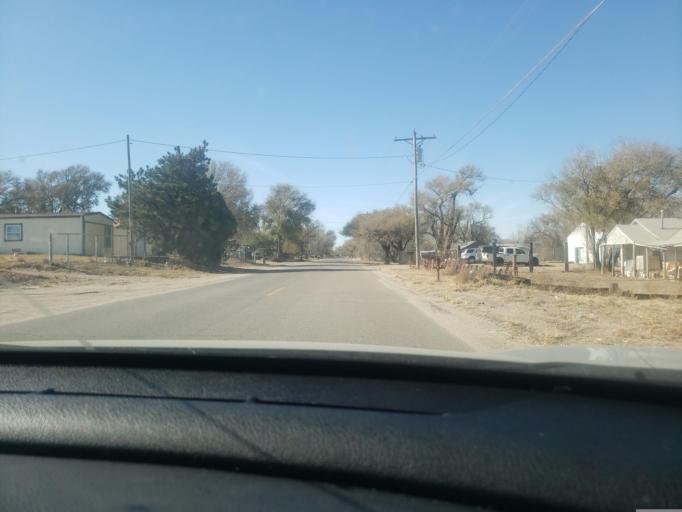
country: US
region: Kansas
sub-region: Finney County
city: Garden City
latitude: 37.9512
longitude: -100.8677
